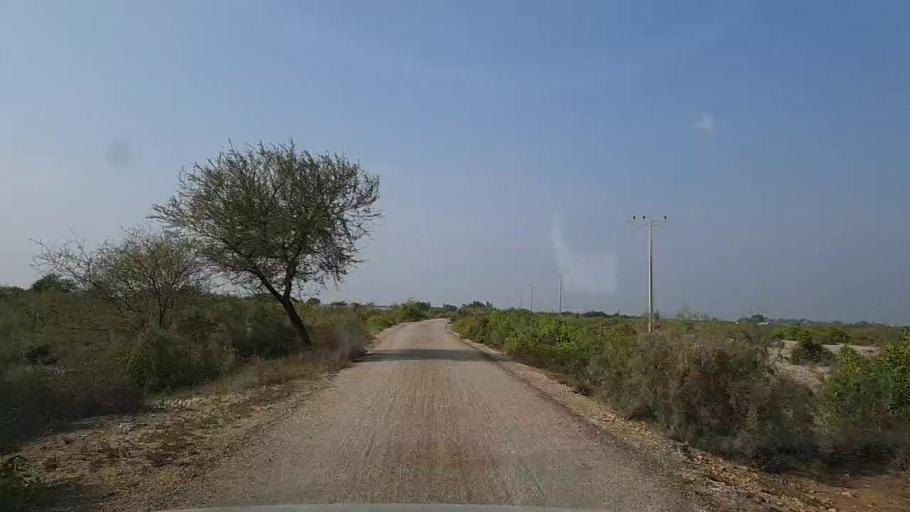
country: PK
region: Sindh
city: Mirpur Sakro
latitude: 24.5761
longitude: 67.5699
